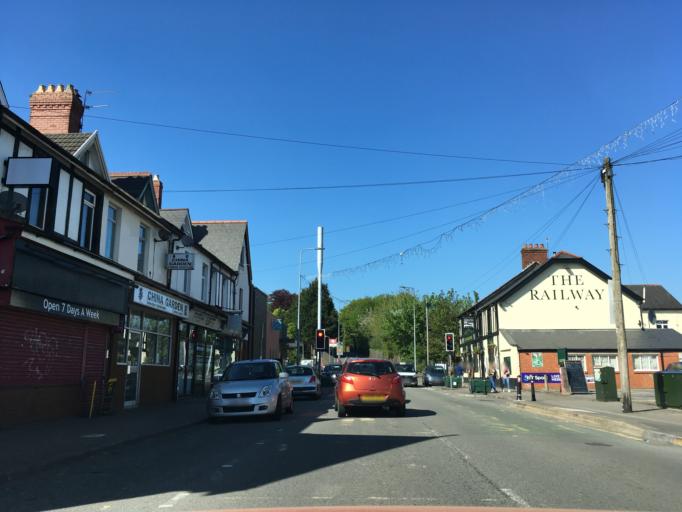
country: GB
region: Wales
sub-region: Cardiff
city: Radyr
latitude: 51.5068
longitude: -3.2284
